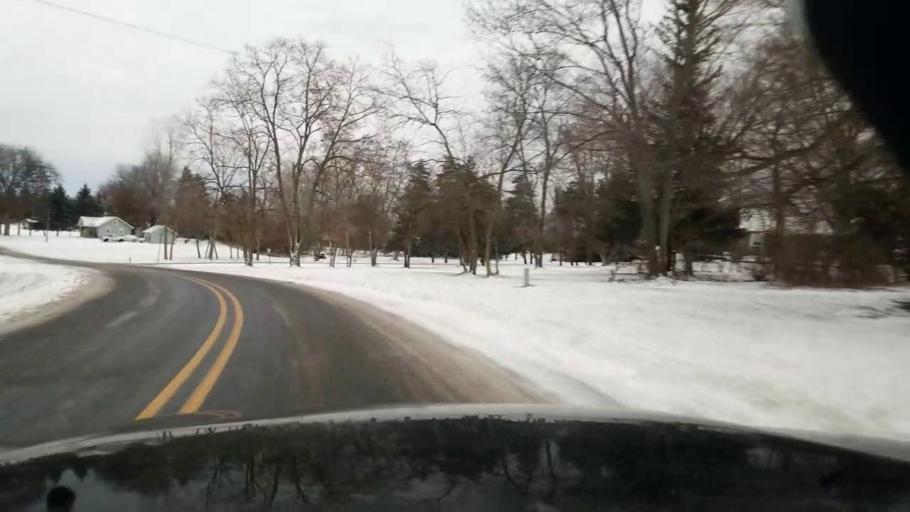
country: US
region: Michigan
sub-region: Jackson County
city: Vandercook Lake
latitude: 42.0948
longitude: -84.4750
